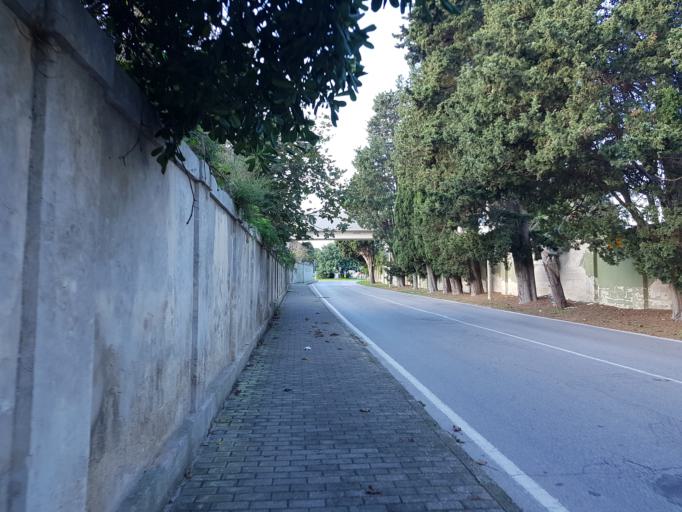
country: IT
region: Apulia
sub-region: Provincia di Brindisi
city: Materdomini
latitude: 40.6503
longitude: 17.9477
